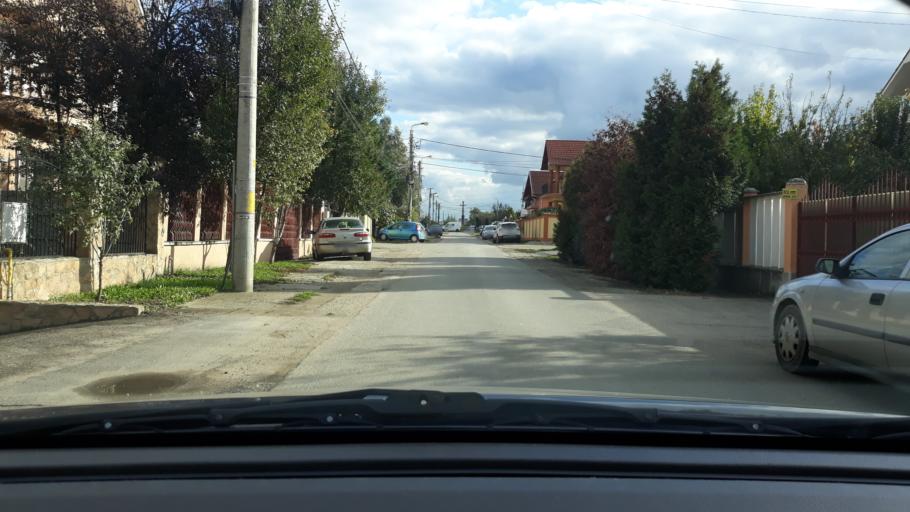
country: RO
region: Bihor
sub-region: Comuna Sanmartin
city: Sanmartin
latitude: 47.0275
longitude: 21.9477
